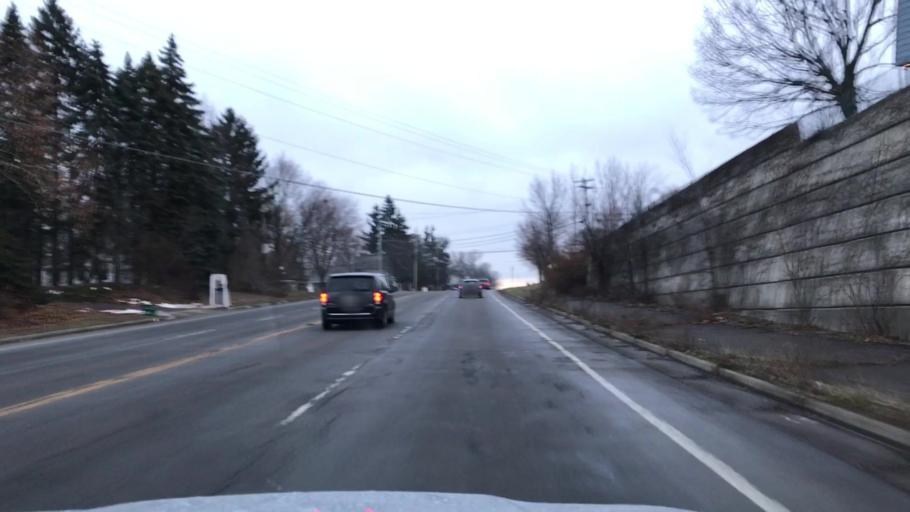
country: US
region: New York
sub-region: Erie County
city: Blasdell
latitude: 42.7927
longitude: -78.7935
